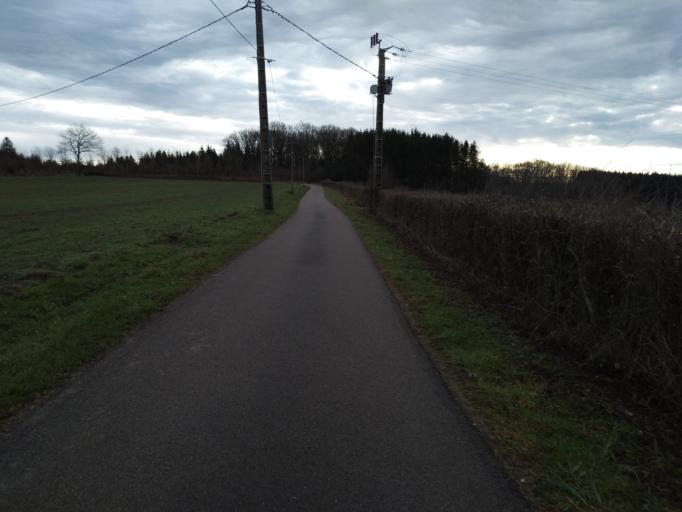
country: FR
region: Bourgogne
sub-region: Departement de la Cote-d'Or
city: Saulieu
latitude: 47.2781
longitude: 4.1558
